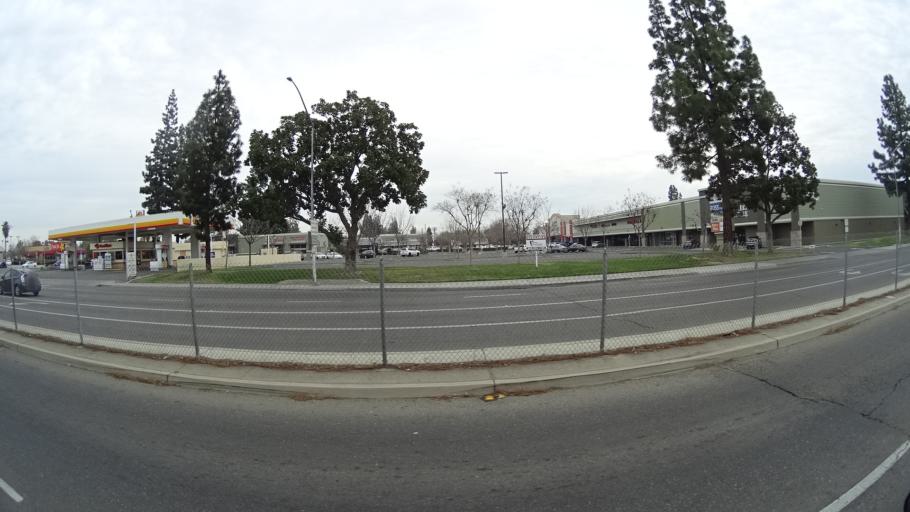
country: US
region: California
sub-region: Fresno County
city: Fresno
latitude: 36.8079
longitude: -119.7725
